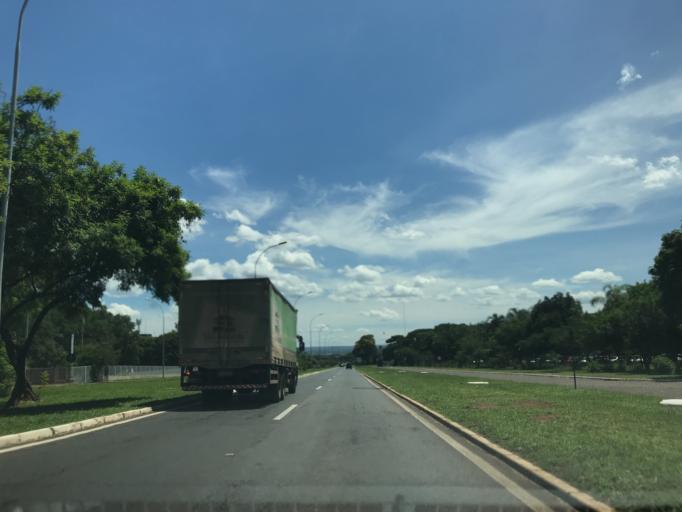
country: BR
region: Federal District
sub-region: Brasilia
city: Brasilia
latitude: -15.7913
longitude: -47.9115
